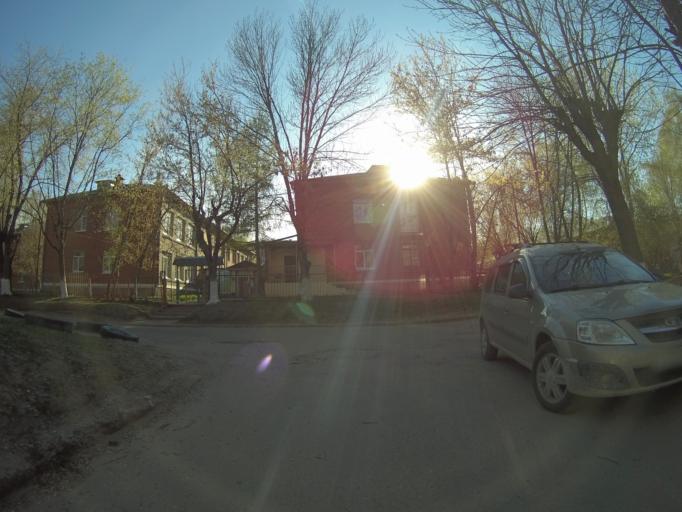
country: RU
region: Vladimir
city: Vladimir
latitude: 56.1491
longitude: 40.4149
